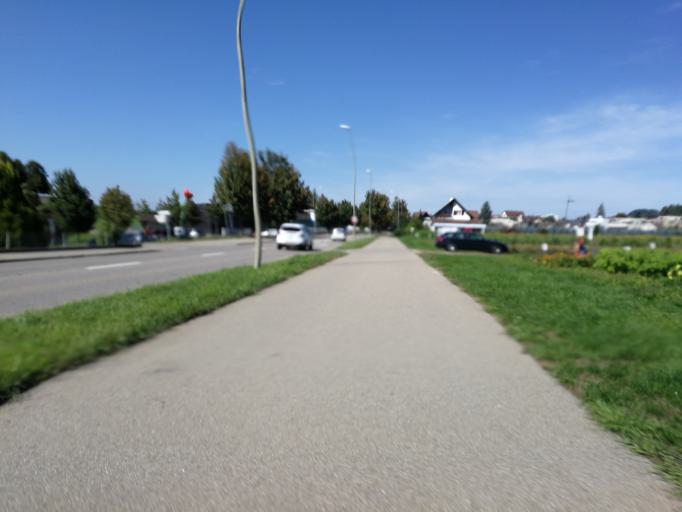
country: CH
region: Zurich
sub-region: Bezirk Pfaeffikon
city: Pfaeffikon / Irgenhausen
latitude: 47.3574
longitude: 8.7970
